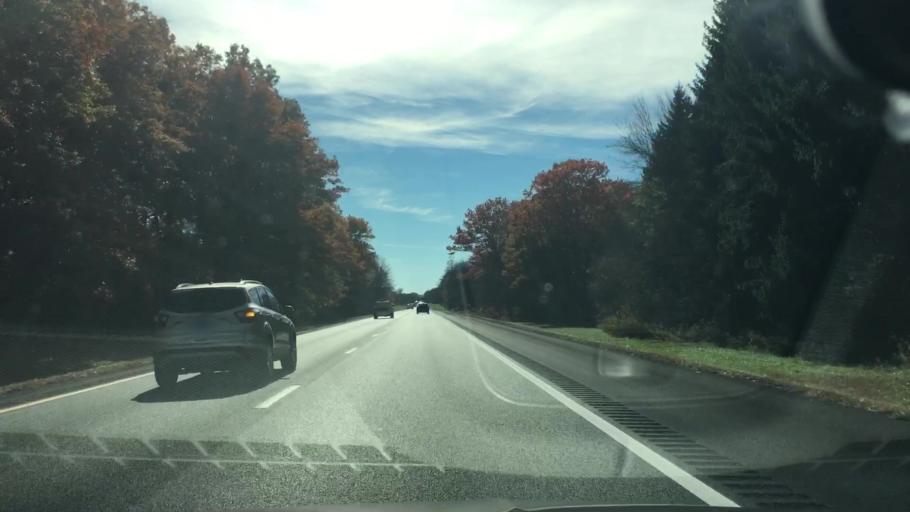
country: US
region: Massachusetts
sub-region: Franklin County
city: Whately
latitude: 42.4215
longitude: -72.6244
